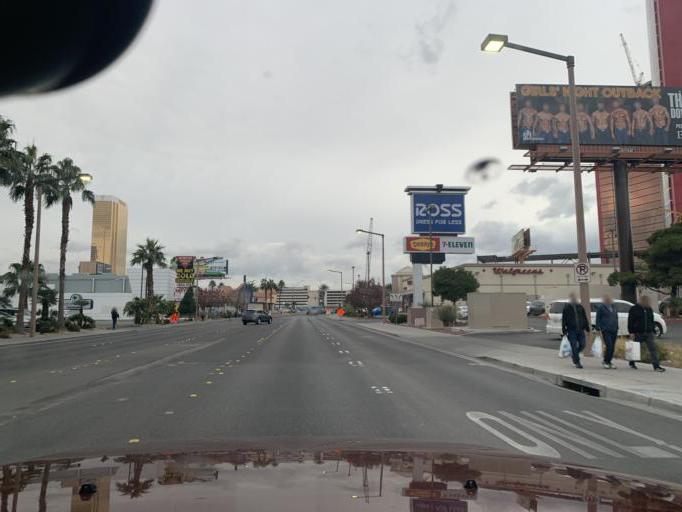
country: US
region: Nevada
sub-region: Clark County
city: Paradise
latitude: 36.1323
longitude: -115.1625
